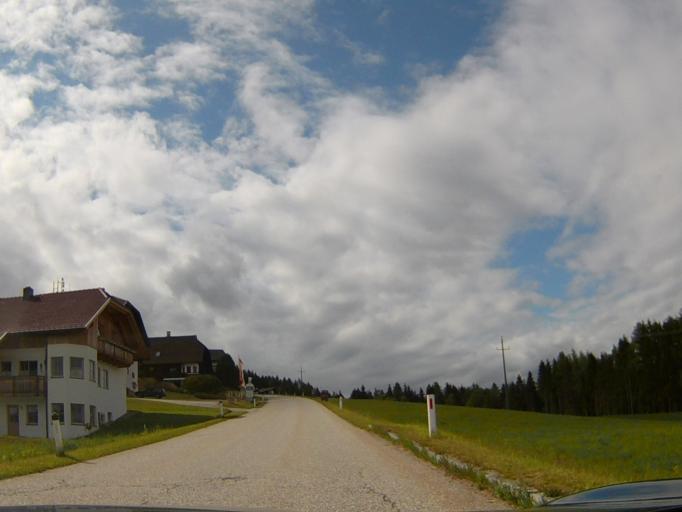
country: AT
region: Carinthia
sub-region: Politischer Bezirk Villach Land
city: Stockenboi
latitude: 46.7363
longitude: 13.5587
